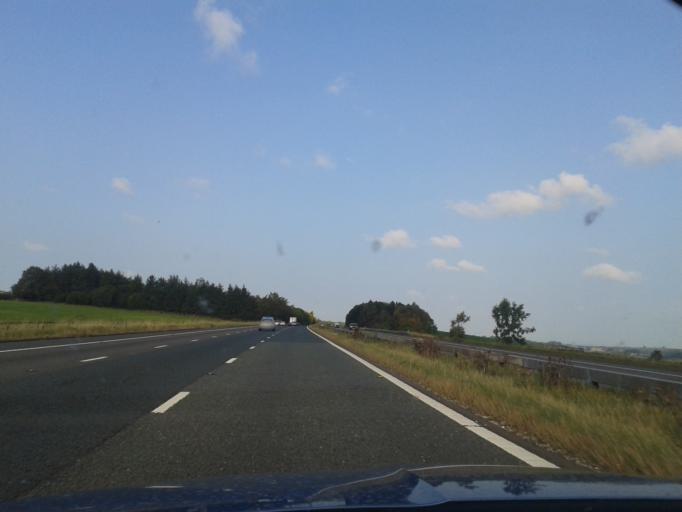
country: GB
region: England
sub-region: Cumbria
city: Scotby
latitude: 54.7673
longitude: -2.8402
